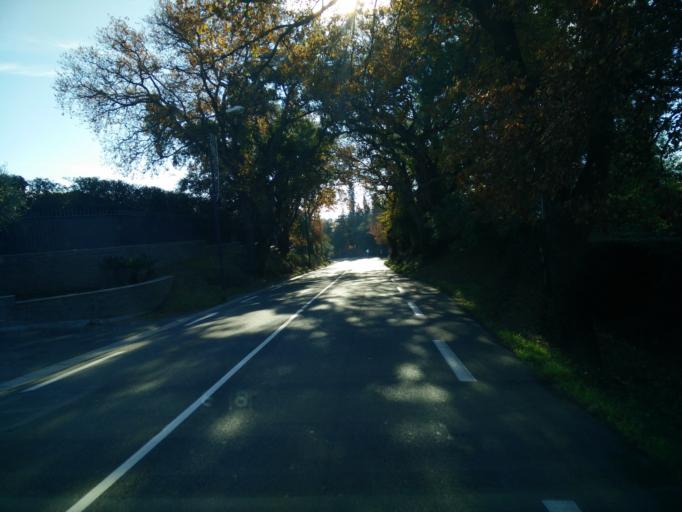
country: FR
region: Provence-Alpes-Cote d'Azur
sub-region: Departement du Var
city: Grimaud
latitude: 43.2706
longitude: 6.5277
